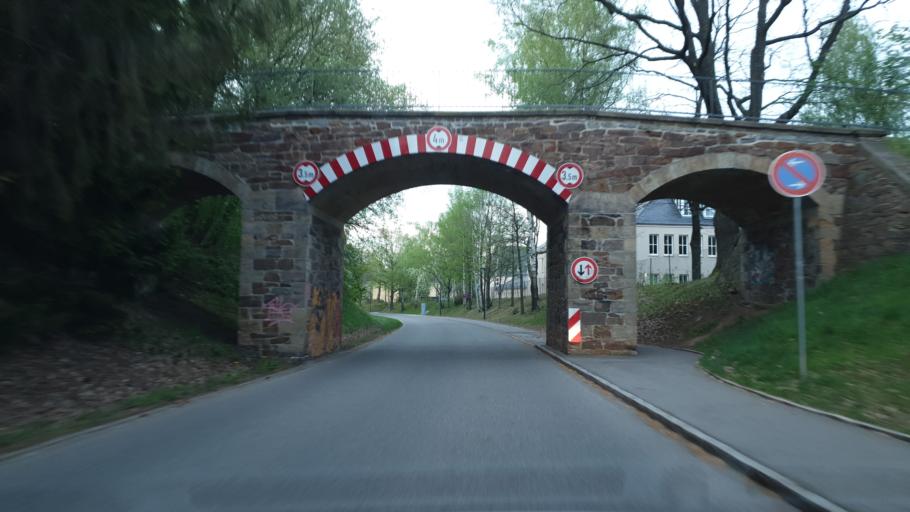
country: DE
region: Saxony
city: Oelsnitz
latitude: 50.7333
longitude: 12.7054
